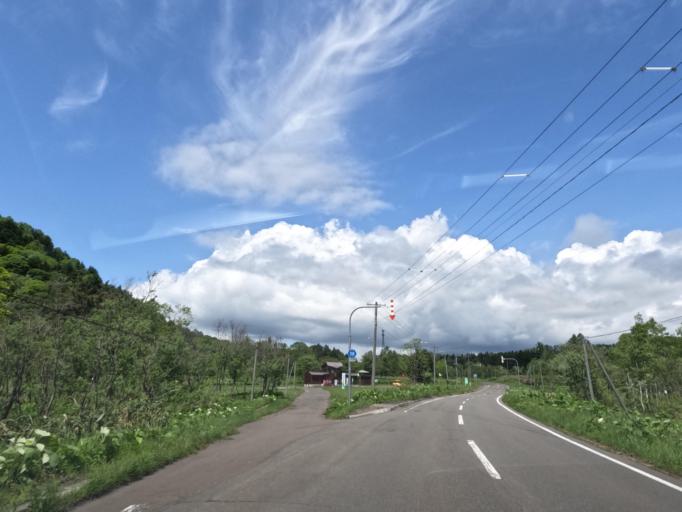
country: JP
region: Hokkaido
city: Tobetsu
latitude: 43.3982
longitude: 141.5806
